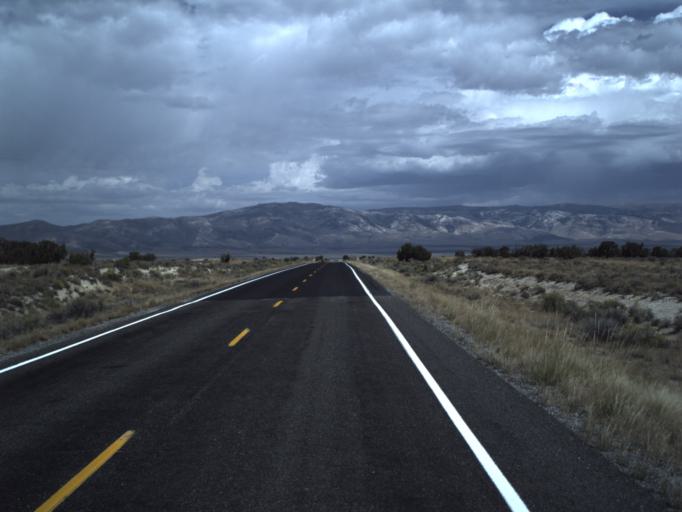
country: US
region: Idaho
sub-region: Cassia County
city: Burley
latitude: 41.7186
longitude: -113.5273
